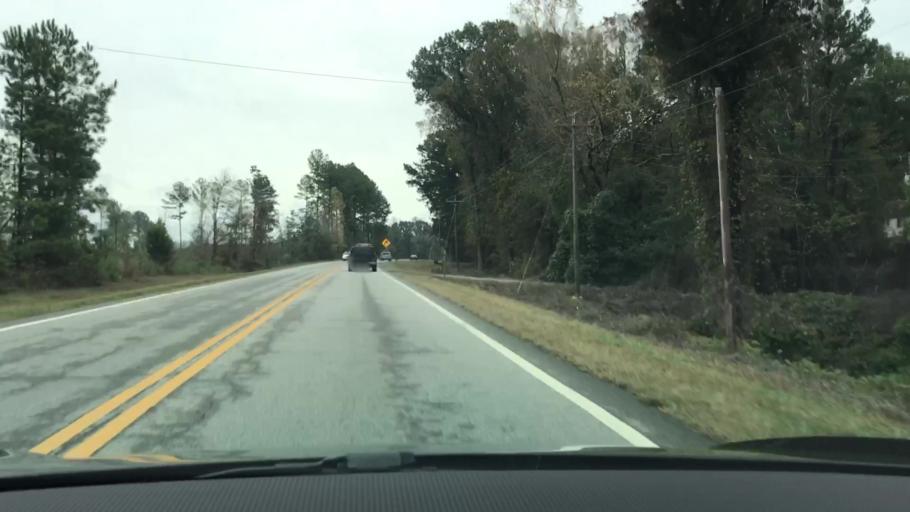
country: US
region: Georgia
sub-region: Greene County
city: Greensboro
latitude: 33.6073
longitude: -83.2012
